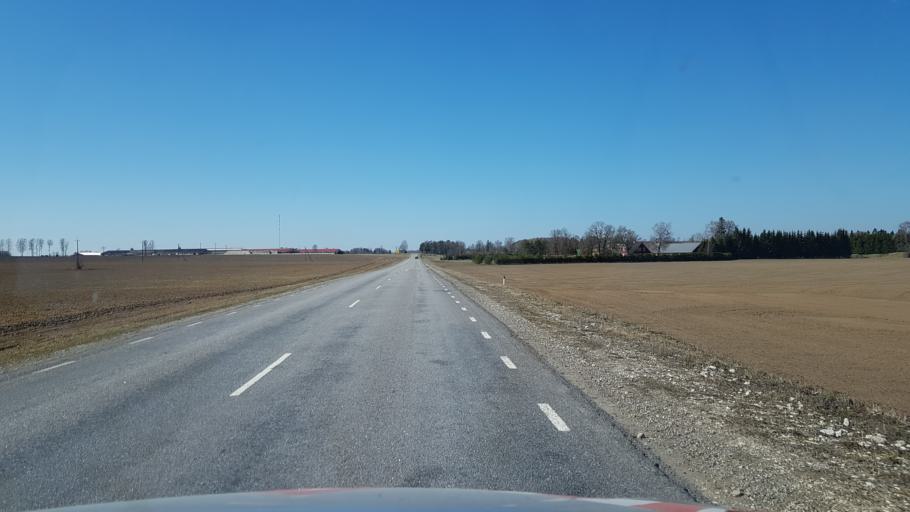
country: EE
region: Laeaene-Virumaa
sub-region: Vaeike-Maarja vald
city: Vaike-Maarja
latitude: 59.1606
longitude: 26.1924
